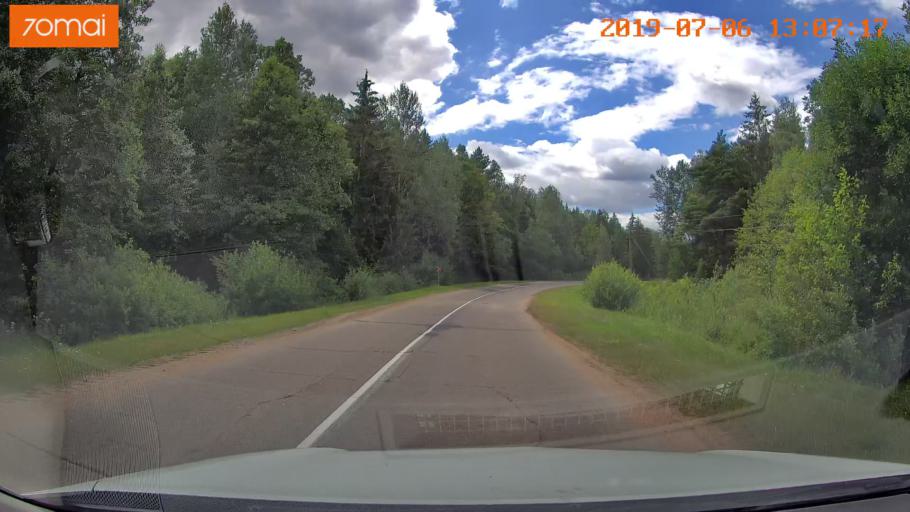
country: BY
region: Minsk
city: Enyerhyetykaw
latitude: 53.6739
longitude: 27.0431
